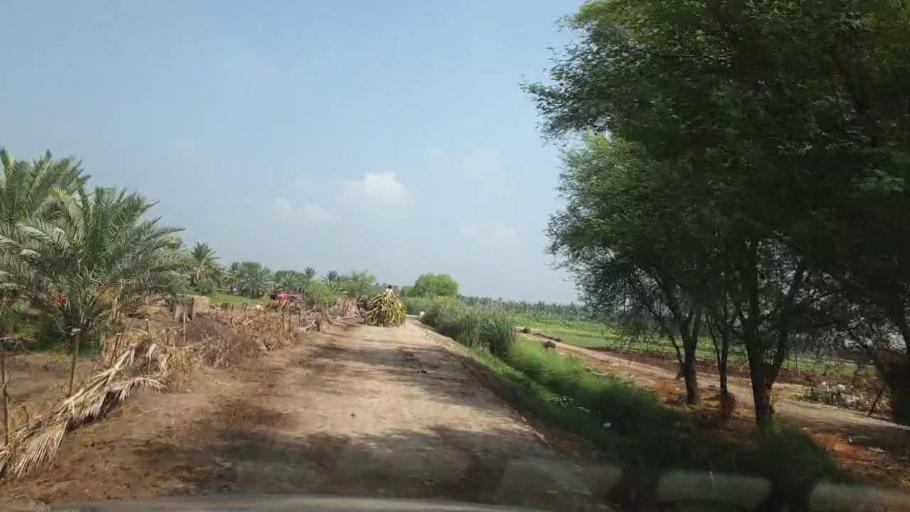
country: PK
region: Sindh
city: Pir jo Goth
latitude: 27.5988
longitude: 68.6934
